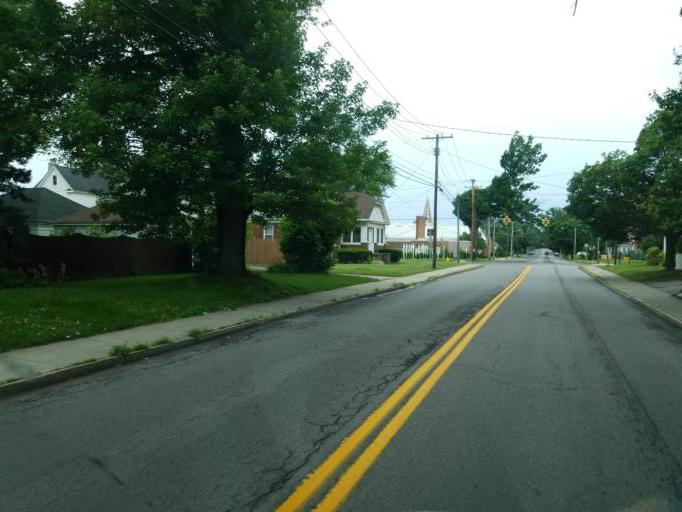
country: CA
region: Ontario
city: Niagara Falls
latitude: 43.1224
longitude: -79.0495
